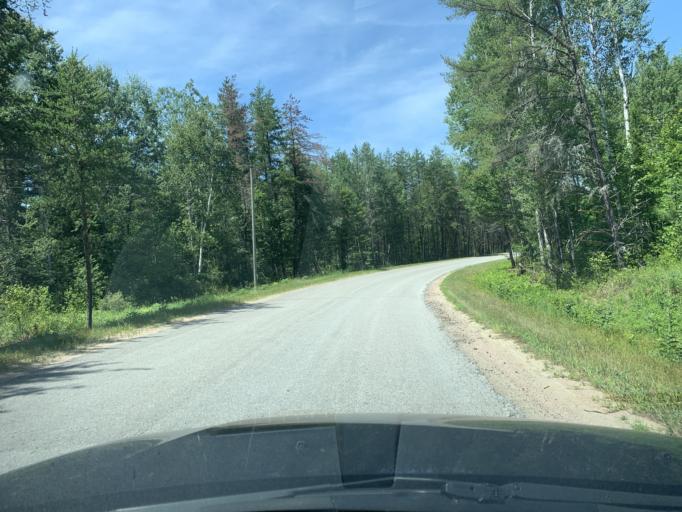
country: CA
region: Ontario
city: Petawawa
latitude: 45.6583
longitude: -77.6045
